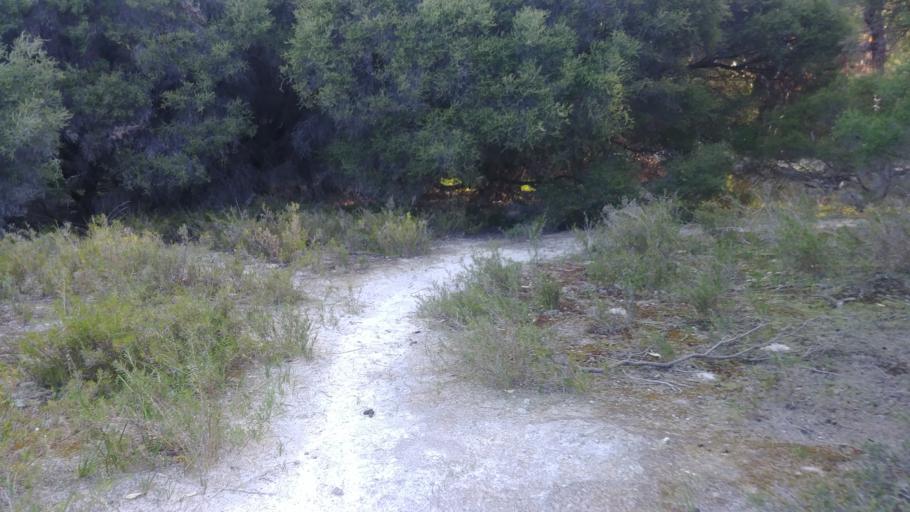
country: AU
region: Western Australia
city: Mosman Park
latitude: -31.9913
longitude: 115.5271
